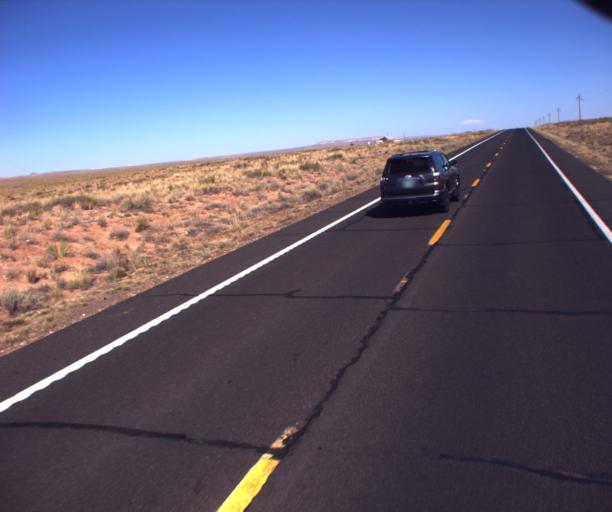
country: US
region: Arizona
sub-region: Coconino County
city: Tuba City
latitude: 36.1429
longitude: -111.1549
